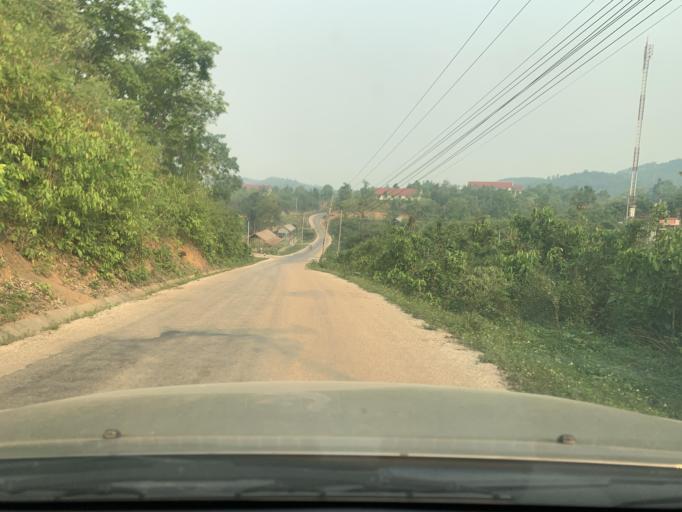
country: LA
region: Louangphabang
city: Louangphabang
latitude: 19.9106
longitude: 102.0808
